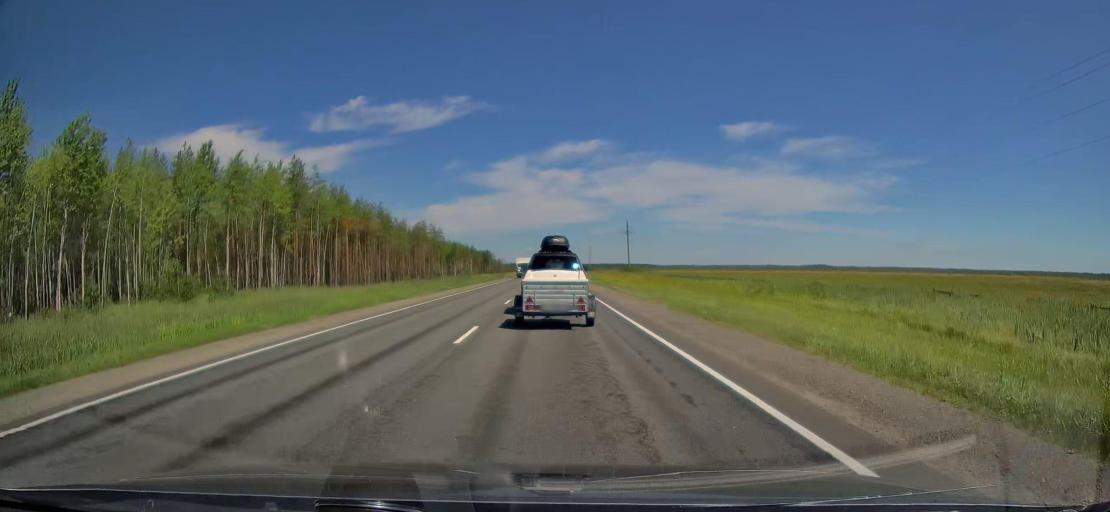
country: RU
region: Vologda
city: Khokhlovo
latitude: 58.9844
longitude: 37.3317
